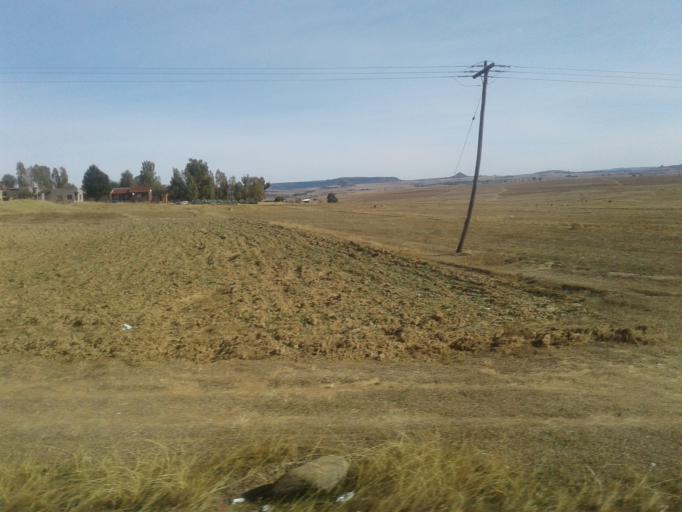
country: LS
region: Berea
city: Teyateyaneng
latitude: -29.0304
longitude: 27.7461
